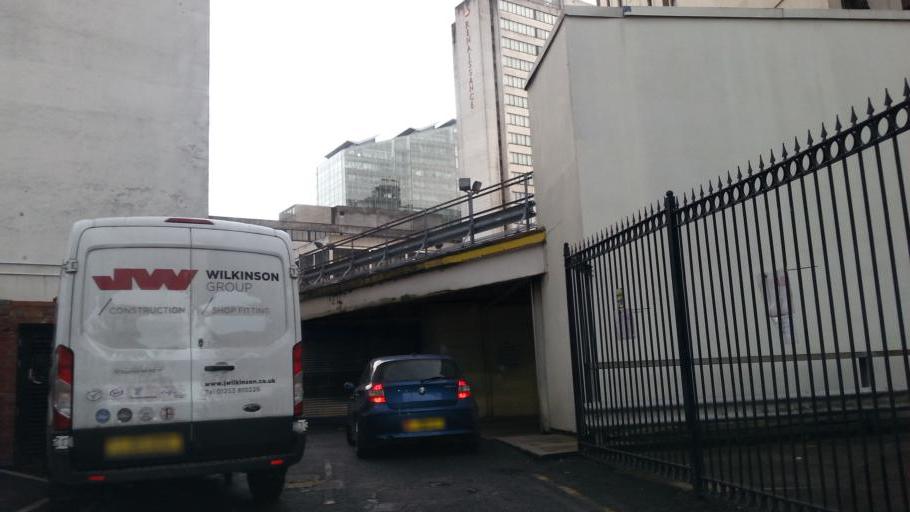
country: GB
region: England
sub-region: Manchester
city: Manchester
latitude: 53.4851
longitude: -2.2473
